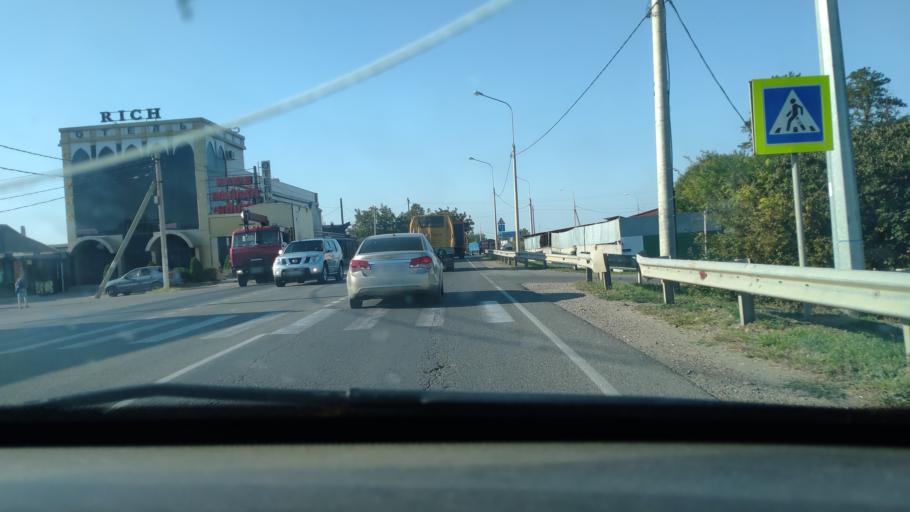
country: RU
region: Krasnodarskiy
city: Novotitarovskaya
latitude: 45.2497
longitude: 38.9951
